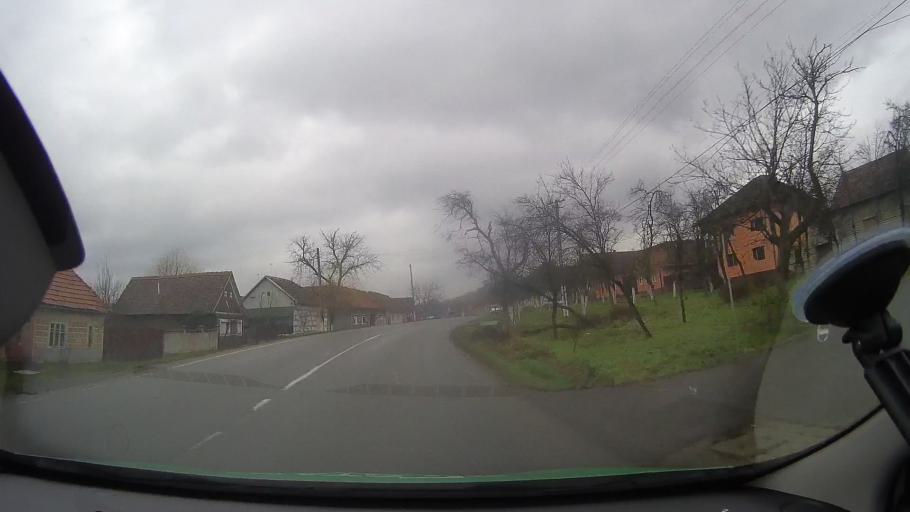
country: RO
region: Arad
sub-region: Comuna Almas
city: Almas
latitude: 46.2998
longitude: 22.1780
